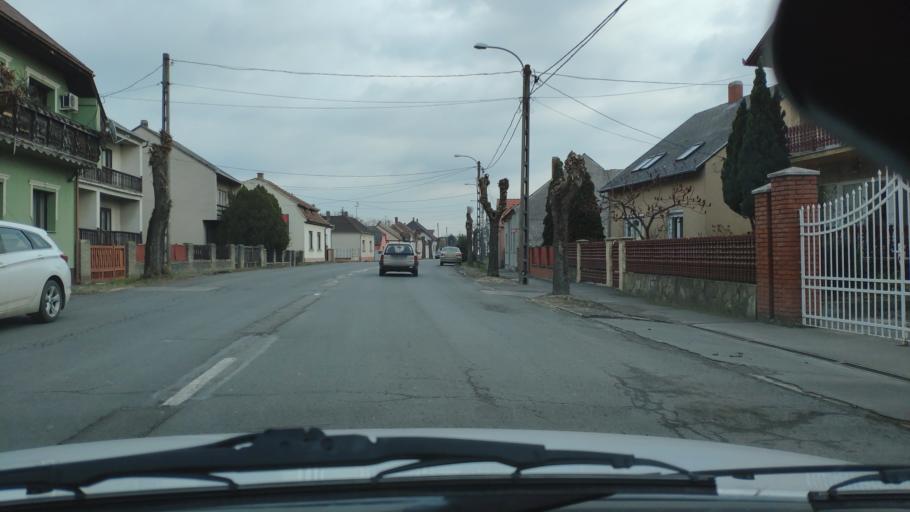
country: HU
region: Zala
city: Nagykanizsa
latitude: 46.4554
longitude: 16.9665
